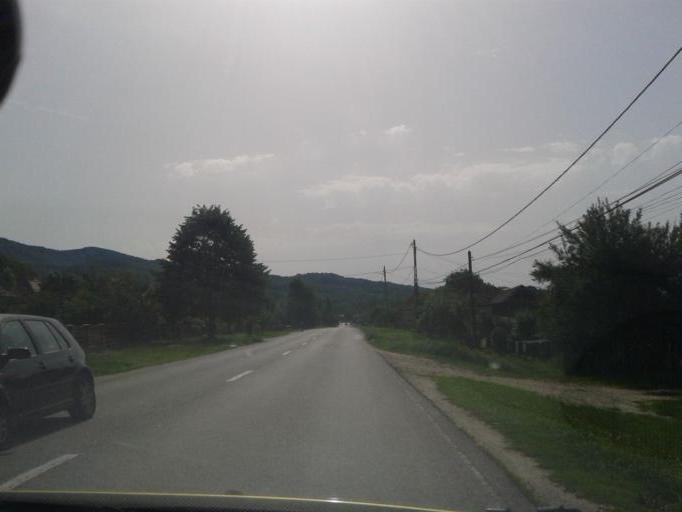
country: RO
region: Valcea
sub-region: Comuna Bunesti
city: Bunesti
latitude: 45.1083
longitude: 24.1906
